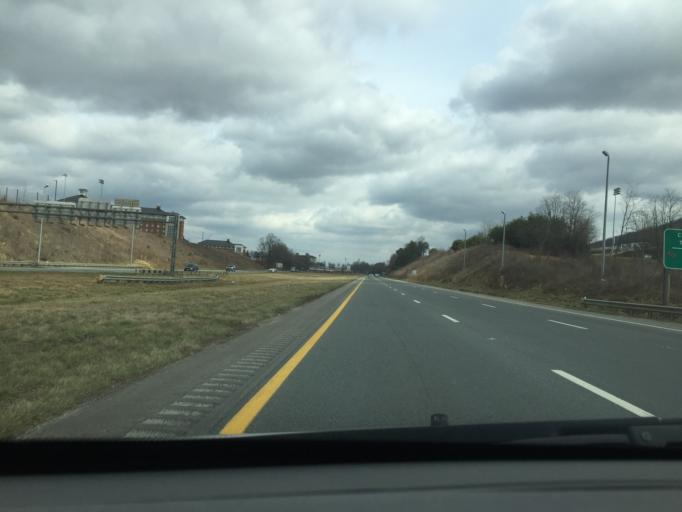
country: US
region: Virginia
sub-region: City of Lynchburg
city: West Lynchburg
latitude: 37.3427
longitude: -79.1837
